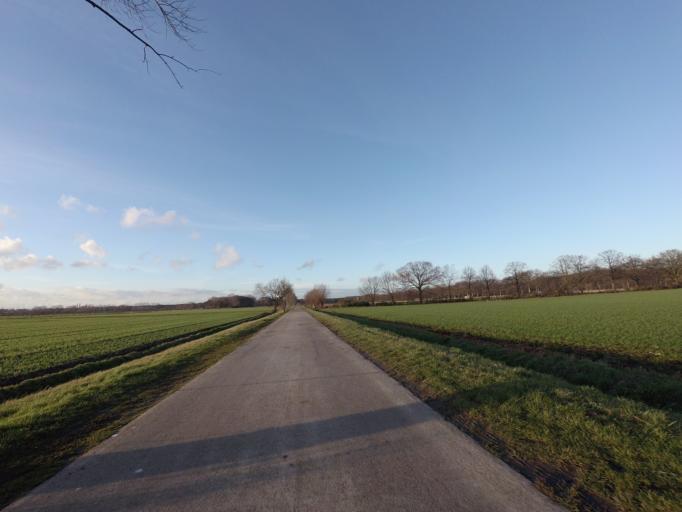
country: BE
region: Flanders
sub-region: Provincie Antwerpen
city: Stabroek
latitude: 51.3449
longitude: 4.3748
